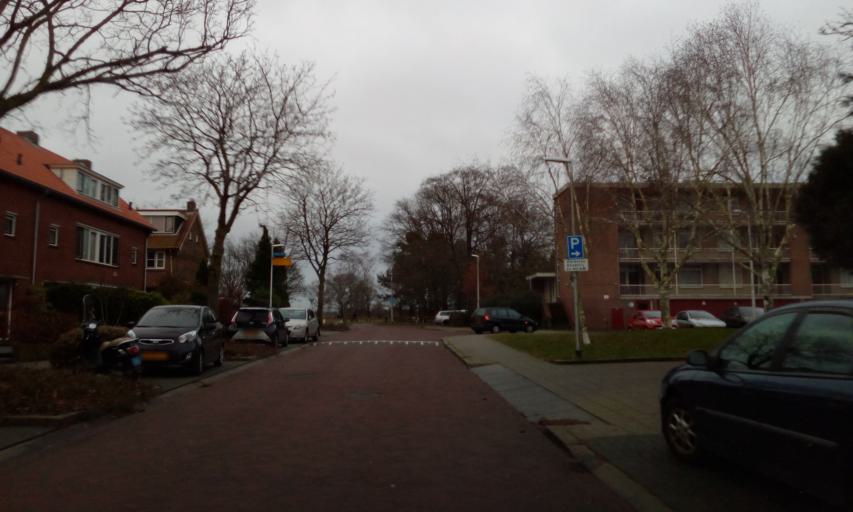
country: NL
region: North Holland
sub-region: Gemeente Bussum
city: Bussum
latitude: 52.2625
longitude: 5.1726
